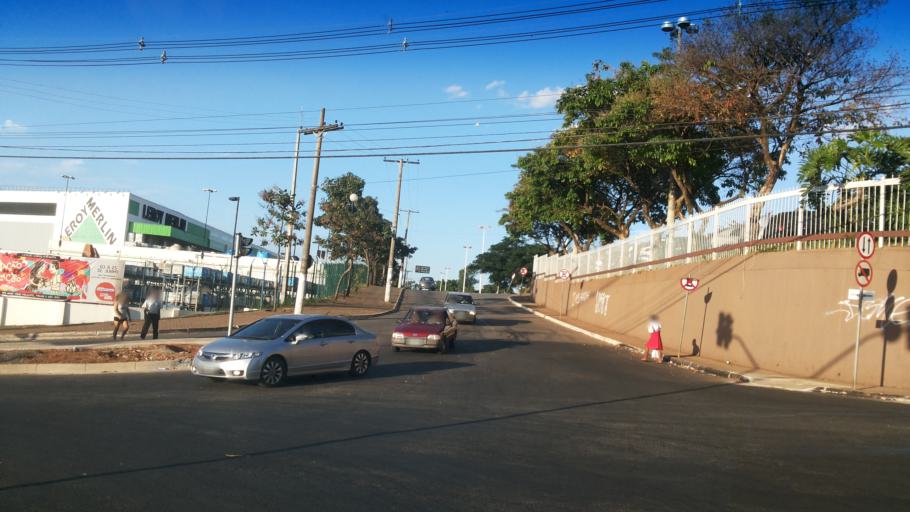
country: BR
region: Goias
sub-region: Goiania
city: Goiania
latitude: -16.6632
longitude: -49.2637
